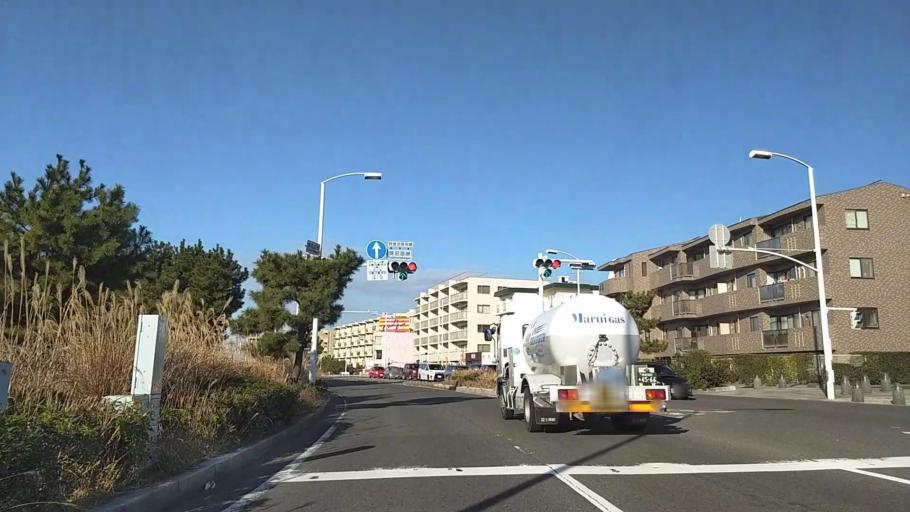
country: JP
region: Kanagawa
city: Fujisawa
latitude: 35.3169
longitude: 139.4709
